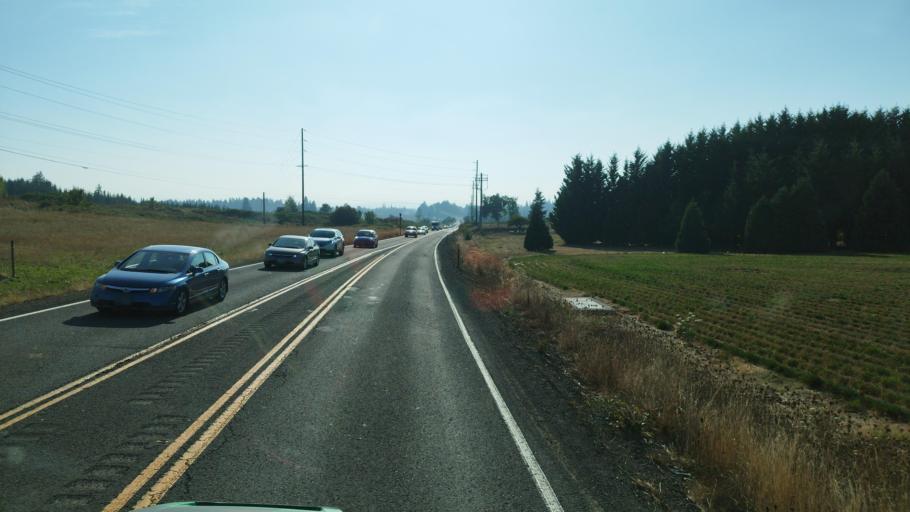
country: US
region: Oregon
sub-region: Washington County
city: Bethany
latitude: 45.5809
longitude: -122.8741
